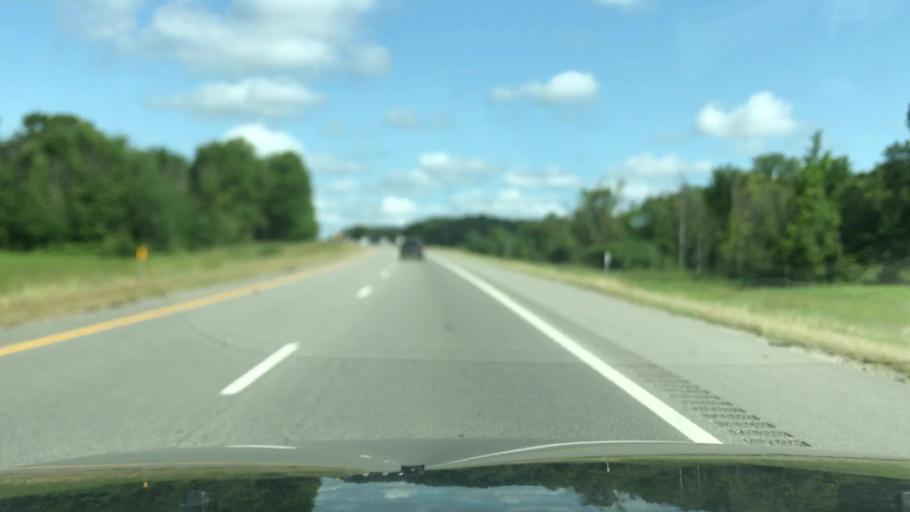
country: US
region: Michigan
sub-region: Mecosta County
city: Big Rapids
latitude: 43.6231
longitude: -85.4990
